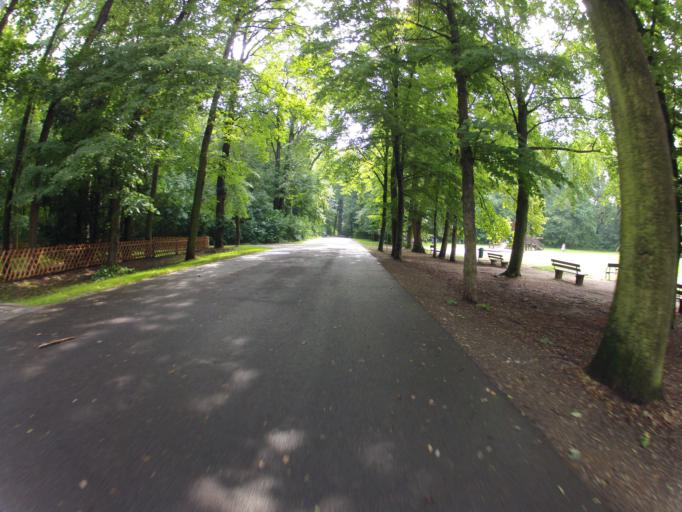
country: DE
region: Saxony
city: Markkleeberg
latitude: 51.2999
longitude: 12.3675
